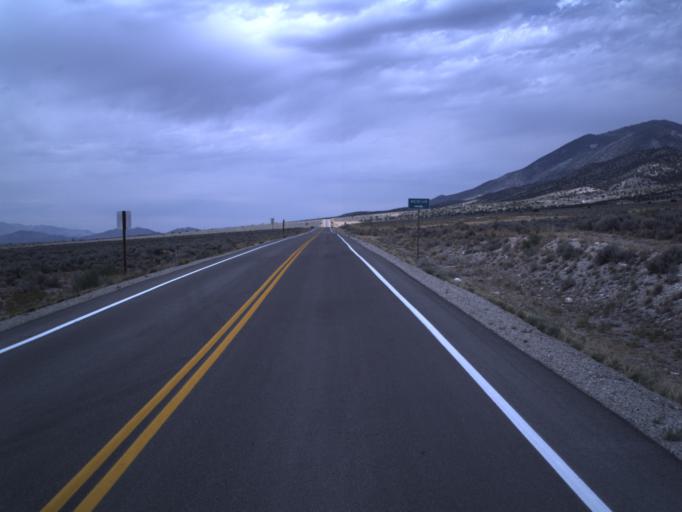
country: US
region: Utah
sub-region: Tooele County
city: Tooele
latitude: 40.2967
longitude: -112.2745
